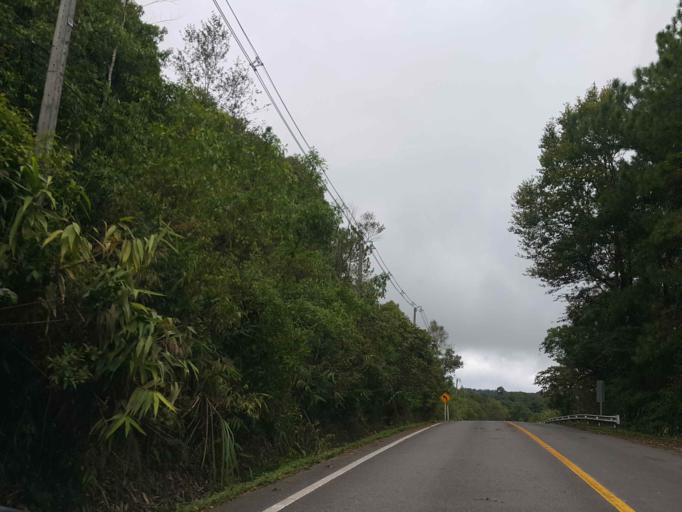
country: TH
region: Chiang Mai
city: Mae Chaem
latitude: 18.5327
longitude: 98.4944
